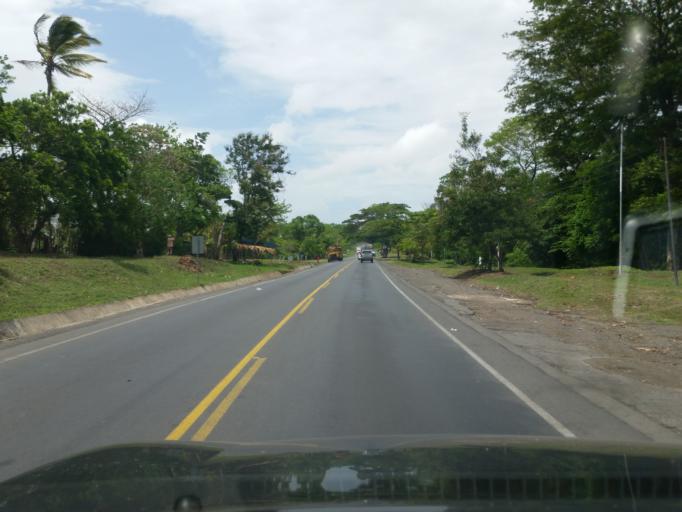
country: NI
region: Masaya
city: Masaya
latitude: 11.9442
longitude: -86.0912
